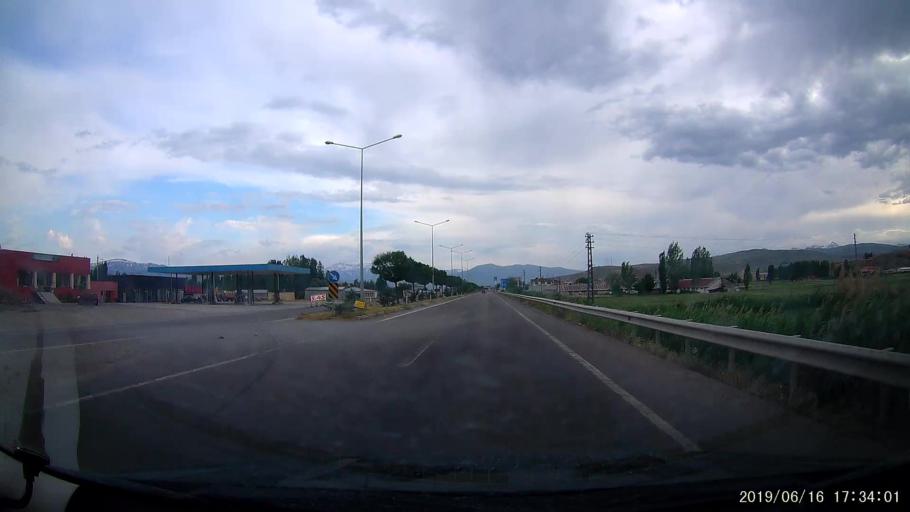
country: TR
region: Erzincan
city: Tercan
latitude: 39.7455
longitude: 40.2732
